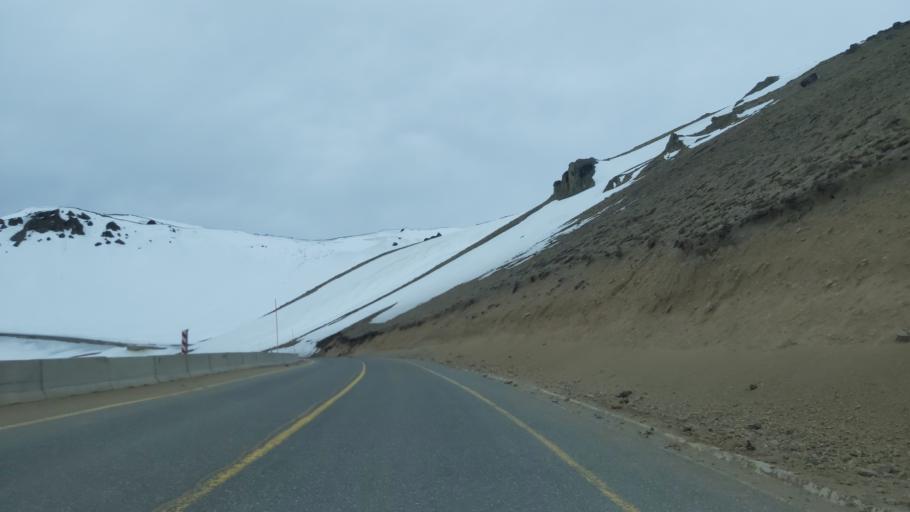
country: CL
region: Maule
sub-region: Provincia de Linares
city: Colbun
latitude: -36.0202
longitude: -70.5032
